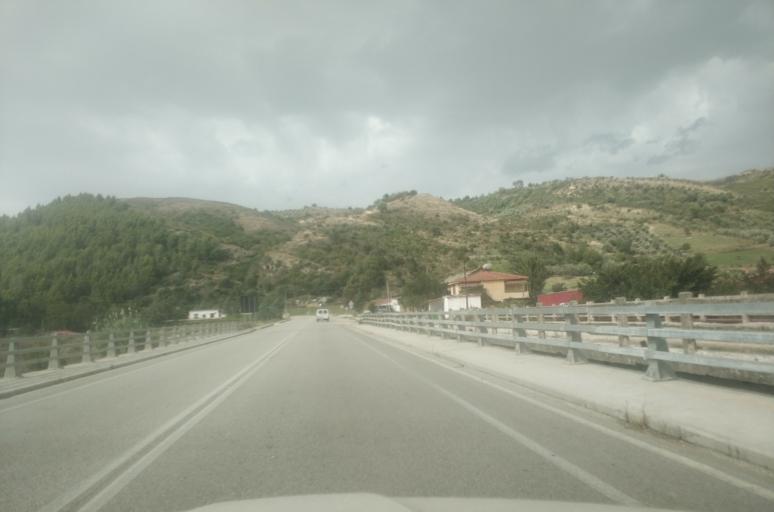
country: AL
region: Gjirokaster
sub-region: Rrethi i Tepelenes
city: Memaliaj
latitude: 40.3514
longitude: 19.9729
